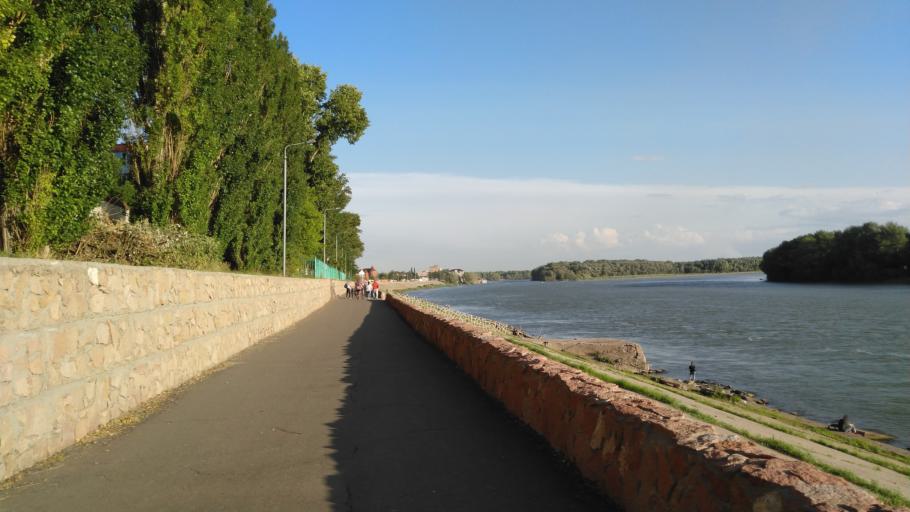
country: KZ
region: Pavlodar
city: Pavlodar
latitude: 52.2769
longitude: 76.9334
